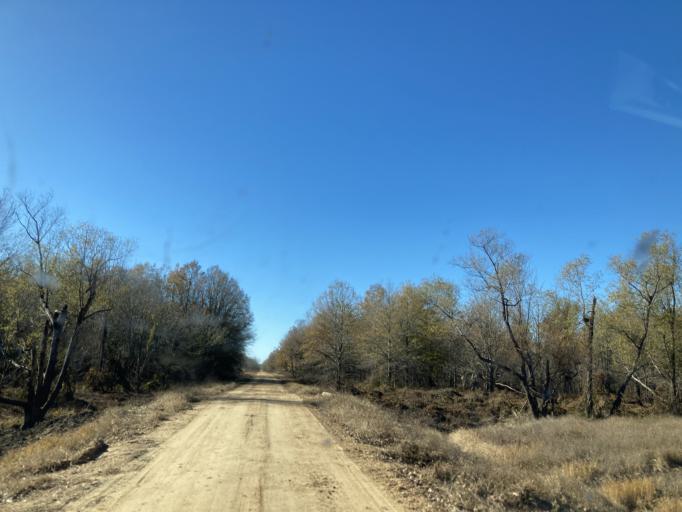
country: US
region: Mississippi
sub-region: Sharkey County
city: Rolling Fork
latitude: 32.7491
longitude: -90.6706
